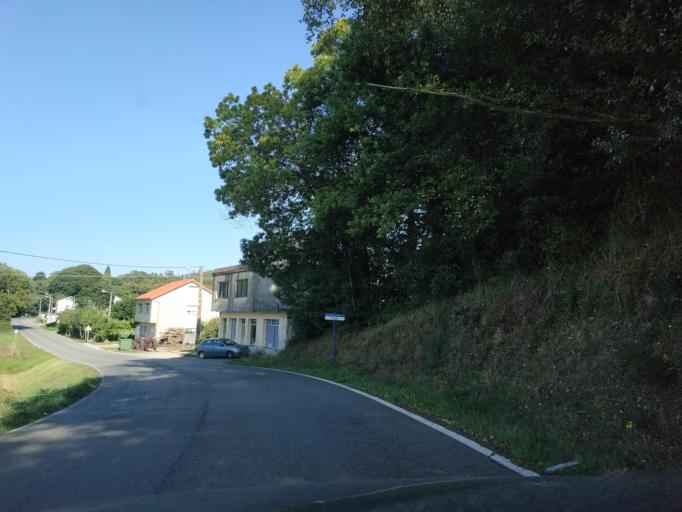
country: ES
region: Galicia
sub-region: Provincia da Coruna
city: Cerceda
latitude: 43.2328
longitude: -8.4881
